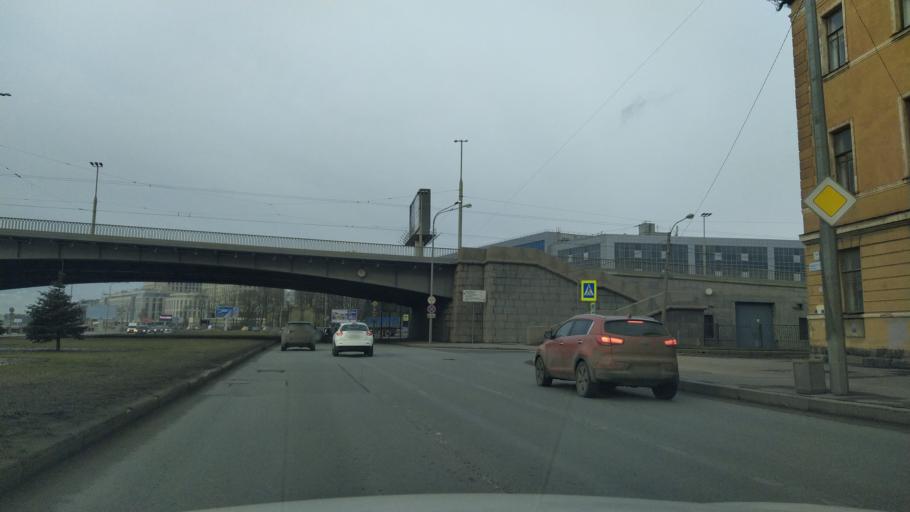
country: RU
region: St.-Petersburg
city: Petrogradka
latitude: 59.9790
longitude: 30.3246
